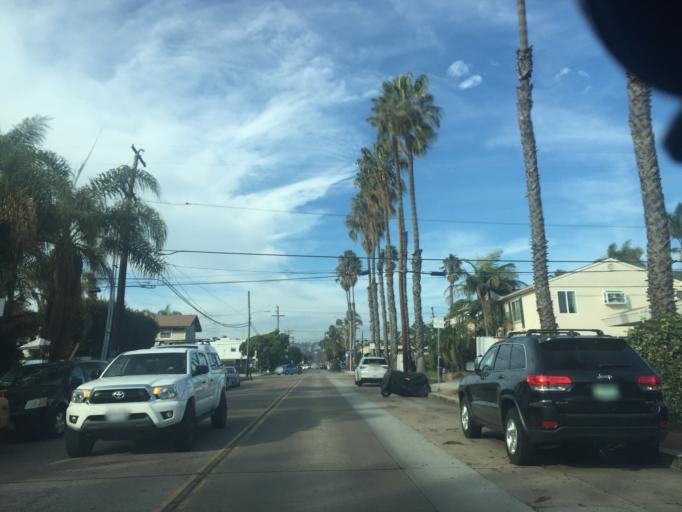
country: US
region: California
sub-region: San Diego County
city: La Jolla
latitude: 32.7970
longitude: -117.2459
